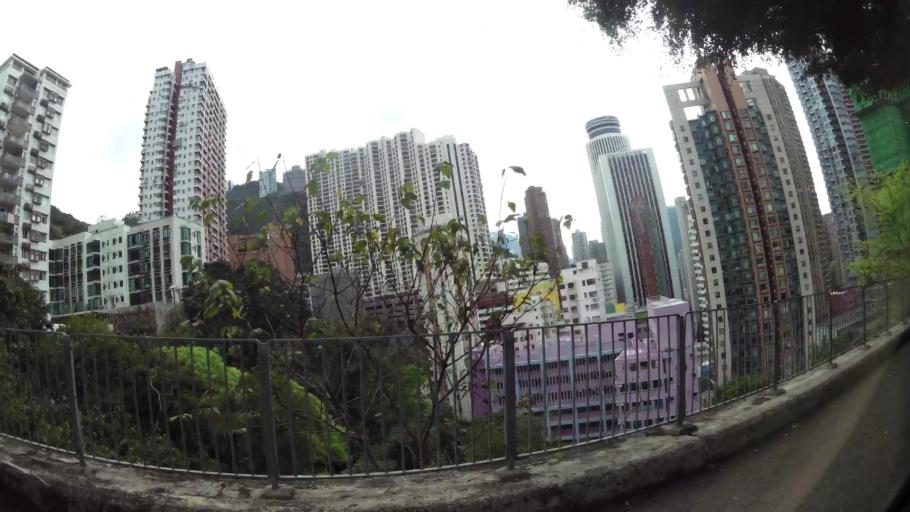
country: HK
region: Wanchai
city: Wan Chai
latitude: 22.2730
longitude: 114.1754
